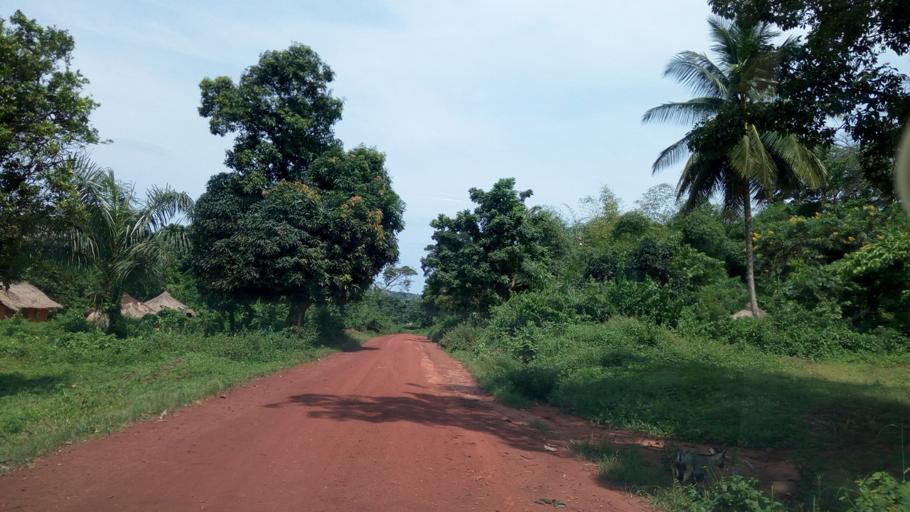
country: CD
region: Equateur
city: Gemena
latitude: 3.2723
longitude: 19.6277
